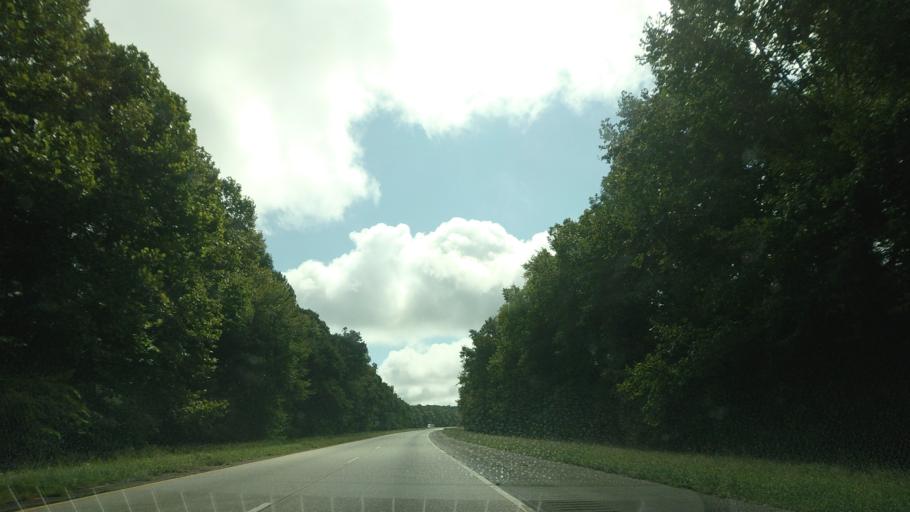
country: US
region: Georgia
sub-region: Twiggs County
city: Jeffersonville
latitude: 32.6489
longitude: -83.4186
